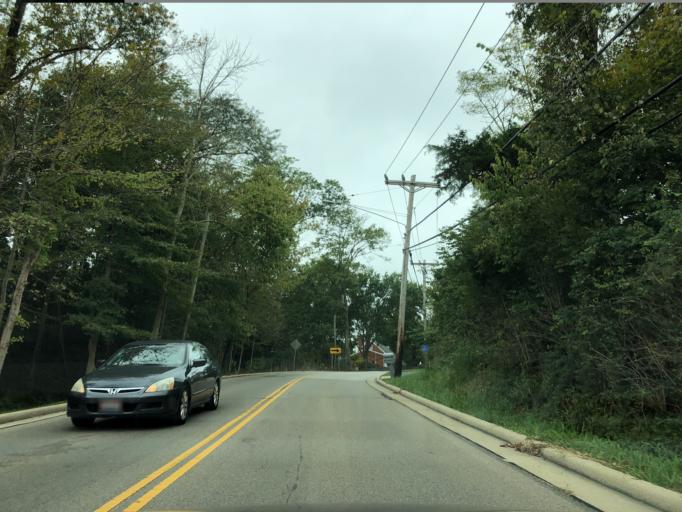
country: US
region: Ohio
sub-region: Hamilton County
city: The Village of Indian Hill
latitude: 39.2677
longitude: -84.2988
